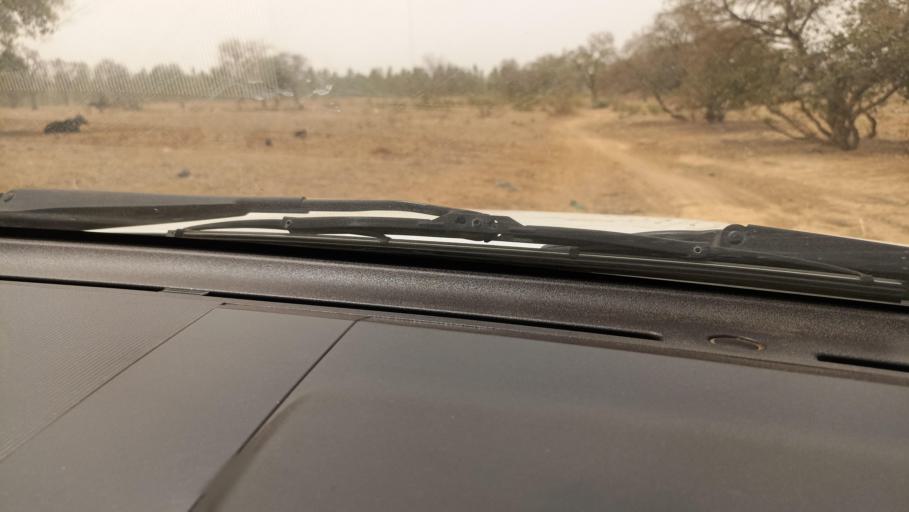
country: BF
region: Boucle du Mouhoun
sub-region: Province du Nayala
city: Toma
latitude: 12.8551
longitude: -2.7975
